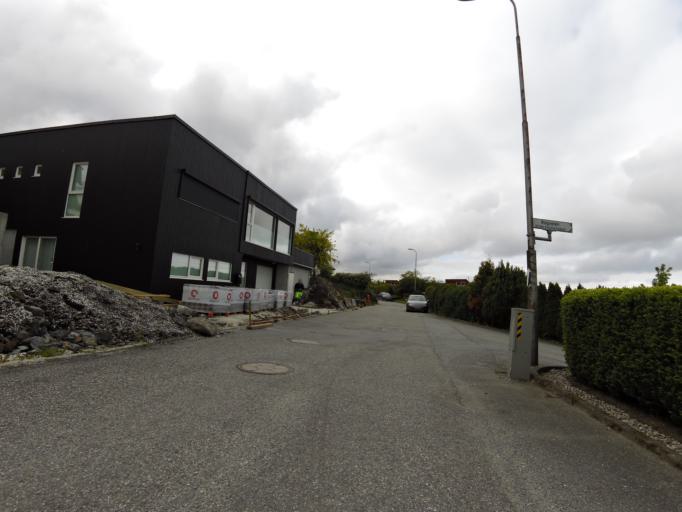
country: NO
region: Rogaland
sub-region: Randaberg
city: Randaberg
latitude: 58.9545
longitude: 5.6602
